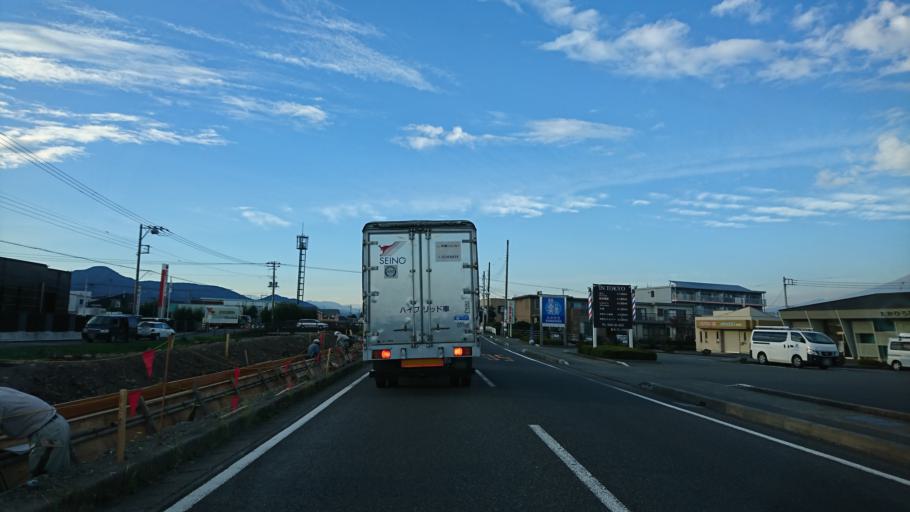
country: JP
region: Shizuoka
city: Fuji
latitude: 35.1414
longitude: 138.6490
